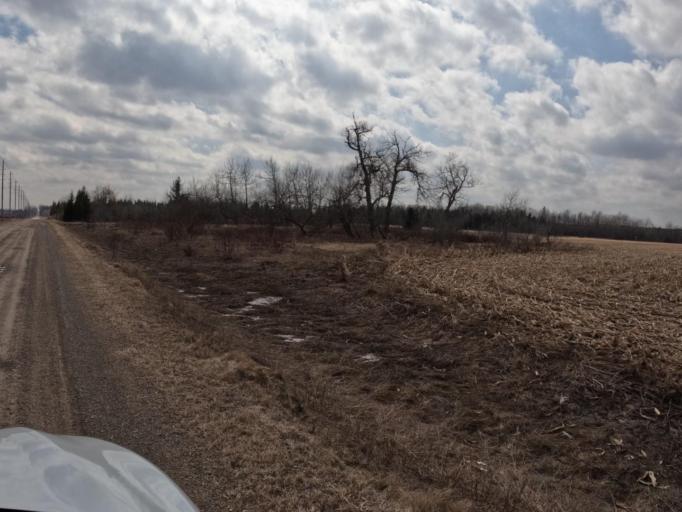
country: CA
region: Ontario
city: Shelburne
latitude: 44.0320
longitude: -80.3158
